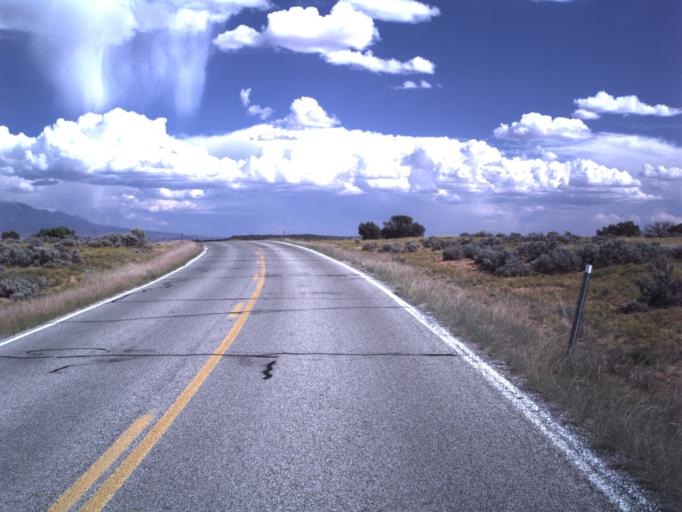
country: US
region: Utah
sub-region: Grand County
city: Moab
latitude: 38.5231
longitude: -109.7418
